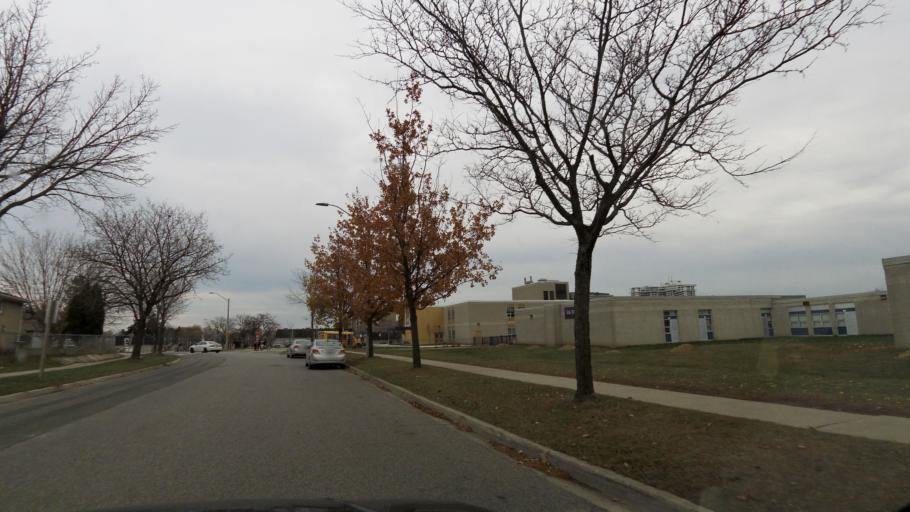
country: CA
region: Ontario
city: Etobicoke
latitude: 43.6228
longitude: -79.5969
